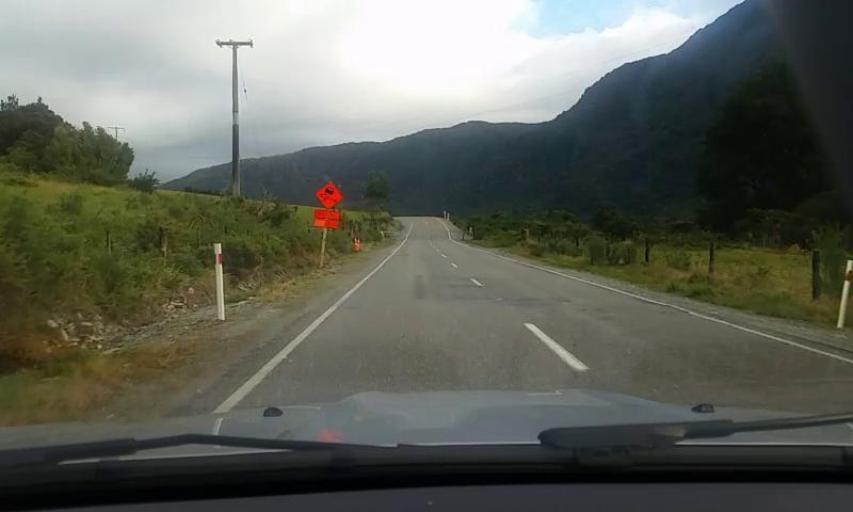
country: NZ
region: West Coast
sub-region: Grey District
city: Greymouth
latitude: -42.7530
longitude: 171.5447
